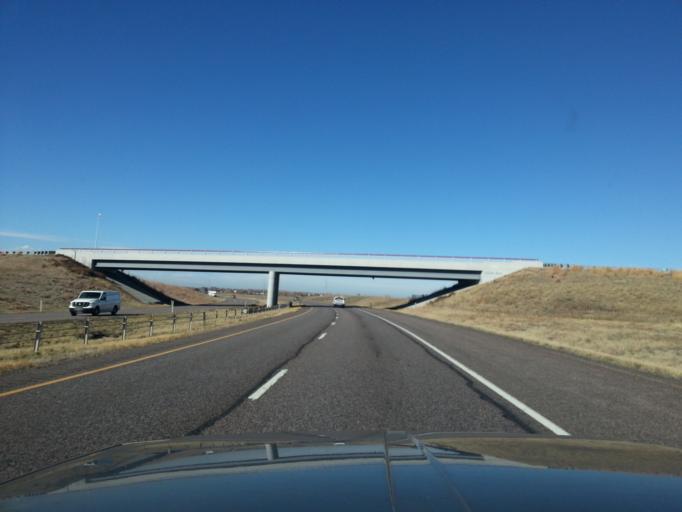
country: US
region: Colorado
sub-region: Adams County
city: Brighton
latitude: 39.8990
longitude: -104.7620
